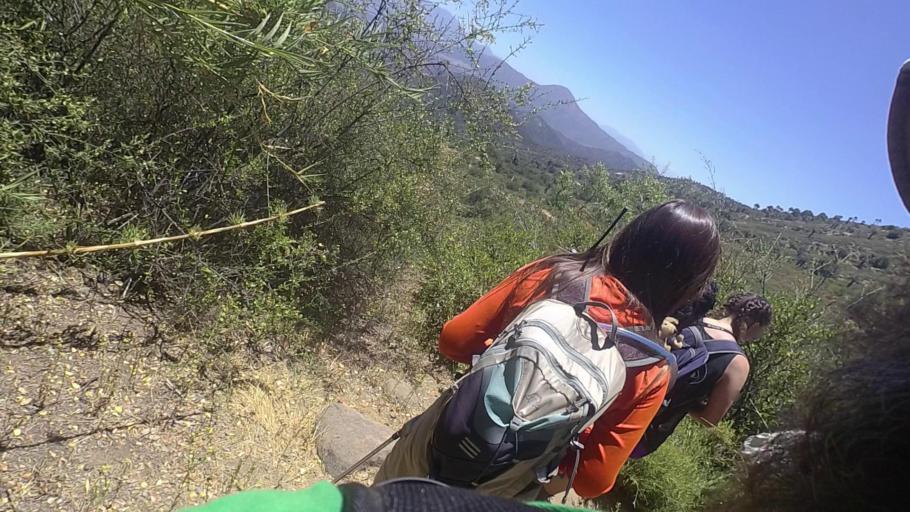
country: CL
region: Valparaiso
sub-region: Provincia de Quillota
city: Quillota
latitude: -32.9713
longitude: -71.0920
